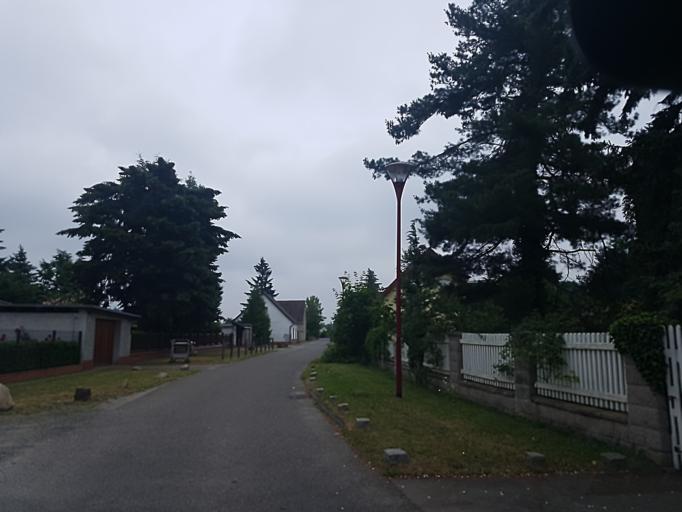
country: DE
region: Brandenburg
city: Finsterwalde
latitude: 51.6316
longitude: 13.7174
